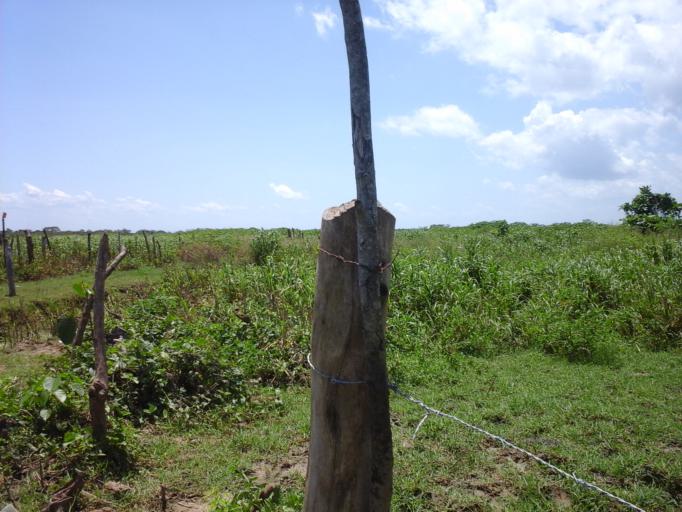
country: CO
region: Bolivar
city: Mahates
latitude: 10.1678
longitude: -75.2743
